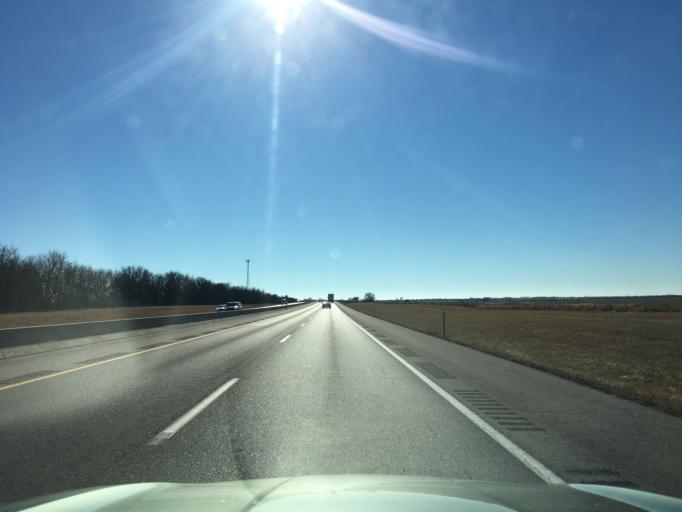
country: US
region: Kansas
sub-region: Sumner County
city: Wellington
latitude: 37.1244
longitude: -97.3389
